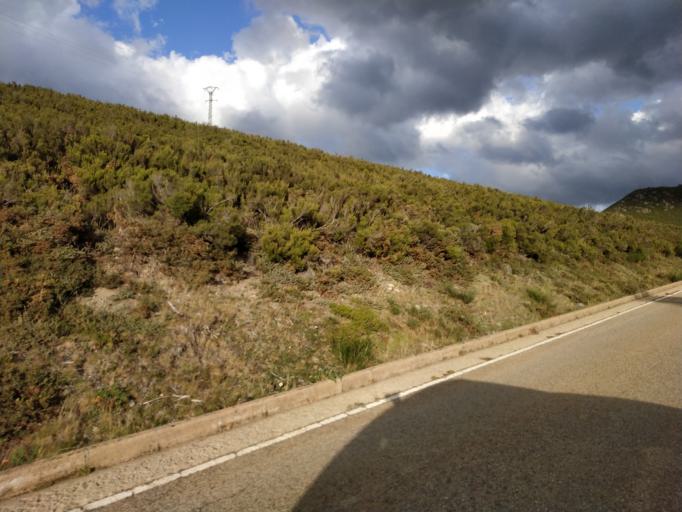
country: ES
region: Castille and Leon
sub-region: Provincia de Leon
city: Candin
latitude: 42.8740
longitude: -6.8258
